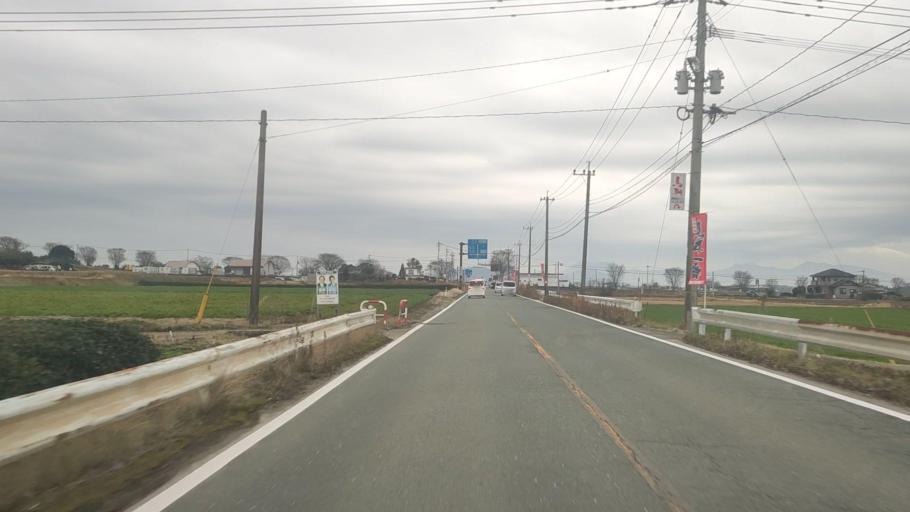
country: JP
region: Kumamoto
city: Ozu
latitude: 32.8483
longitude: 130.8390
